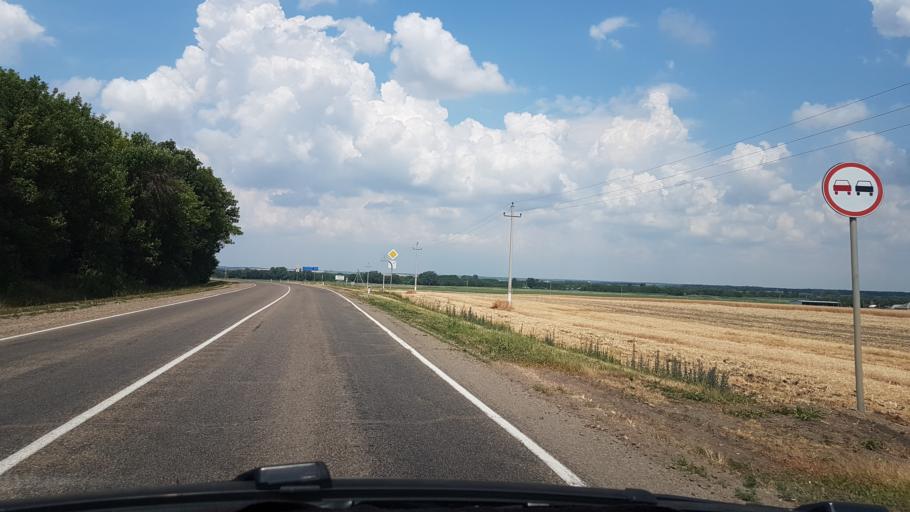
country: RU
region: Krasnodarskiy
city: Dmitriyevskaya
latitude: 45.6967
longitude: 40.7443
